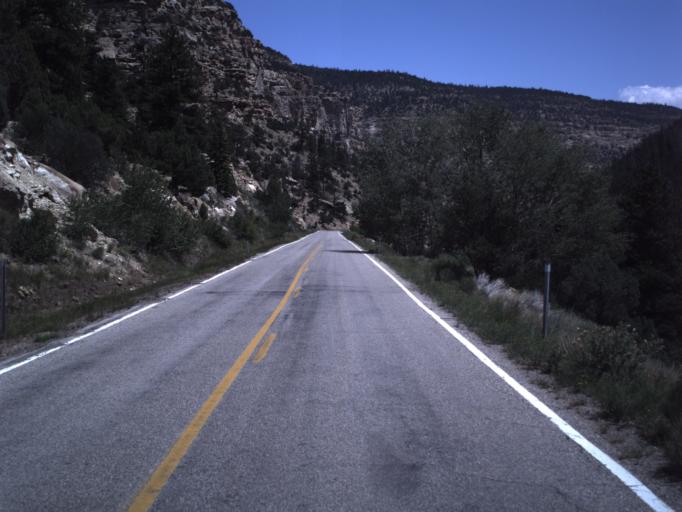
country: US
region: Utah
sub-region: Emery County
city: Orangeville
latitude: 39.2890
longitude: -111.2603
